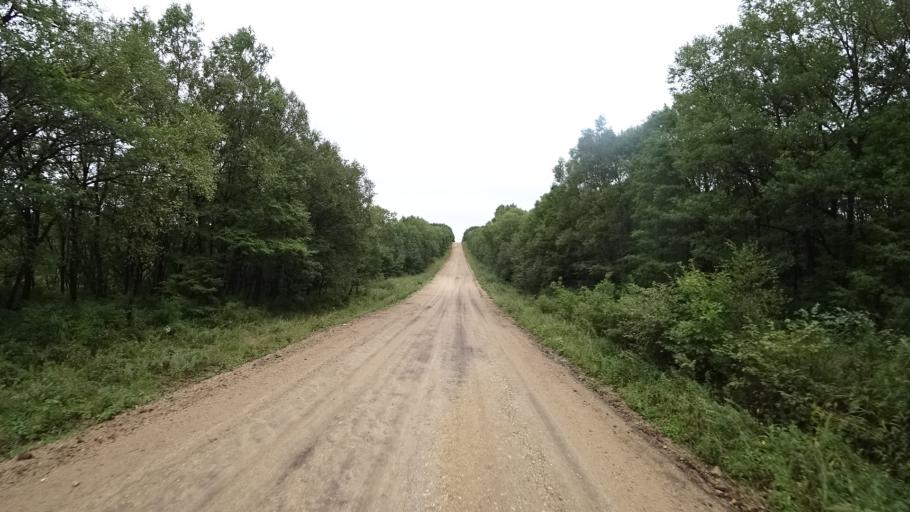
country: RU
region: Primorskiy
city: Ivanovka
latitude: 44.0449
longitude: 132.5432
